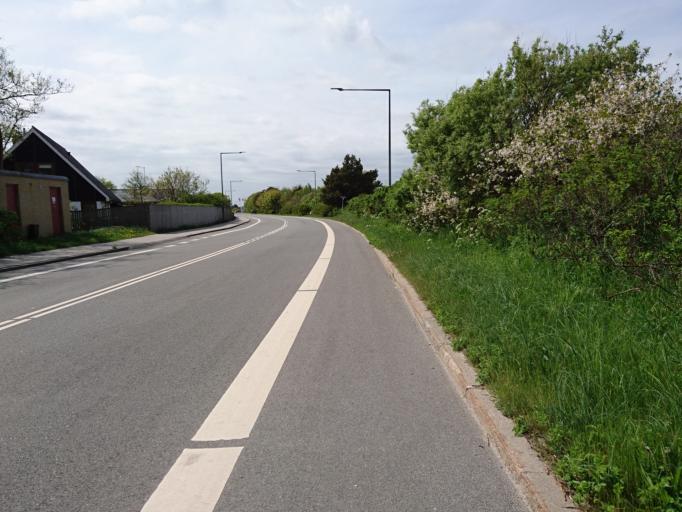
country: DK
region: North Denmark
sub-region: Frederikshavn Kommune
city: Skagen
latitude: 57.7292
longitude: 10.5562
